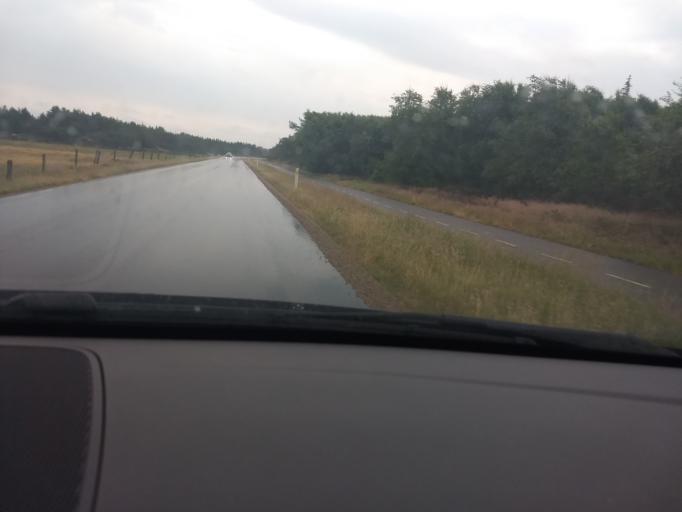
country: DK
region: South Denmark
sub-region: Fano Kommune
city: Nordby
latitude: 55.4070
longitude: 8.4158
